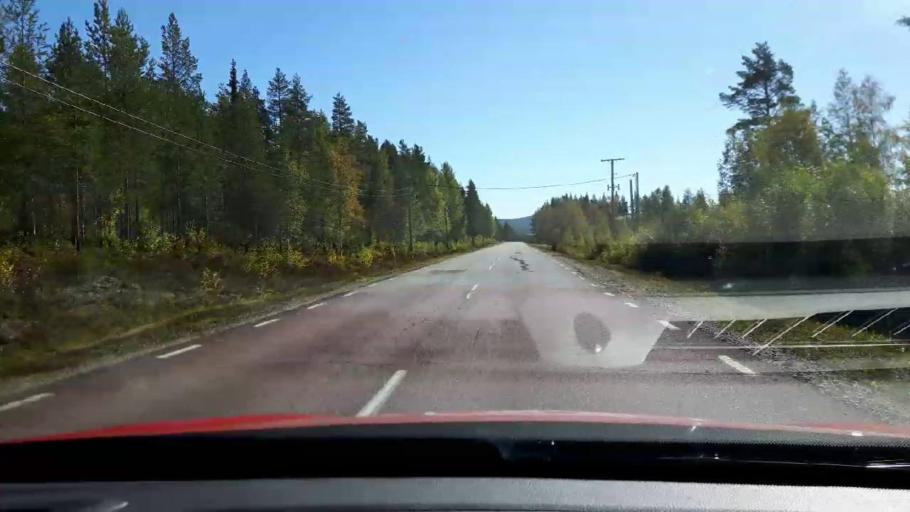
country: SE
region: Jaemtland
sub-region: Harjedalens Kommun
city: Sveg
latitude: 62.2998
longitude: 14.0666
